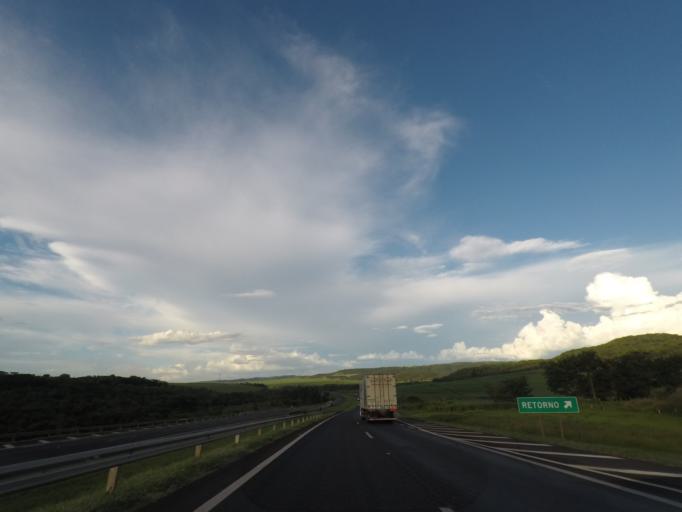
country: BR
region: Sao Paulo
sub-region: Ituverava
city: Ituverava
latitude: -20.2415
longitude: -47.7961
